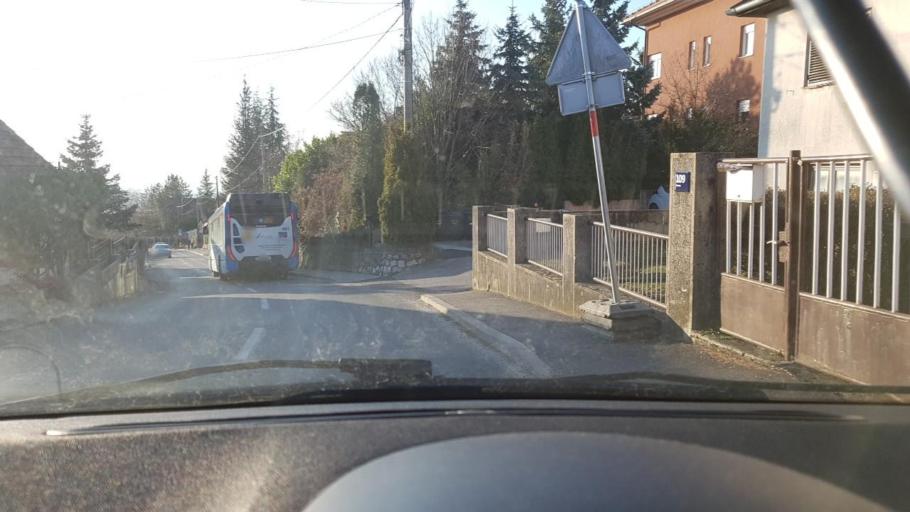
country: HR
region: Grad Zagreb
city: Zagreb
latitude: 45.8500
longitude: 15.9888
